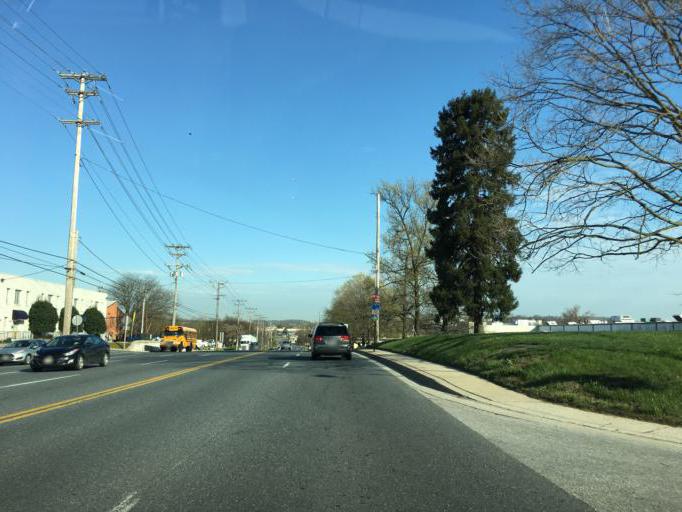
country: US
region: Maryland
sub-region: Baltimore County
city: Cockeysville
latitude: 39.4760
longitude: -76.6513
